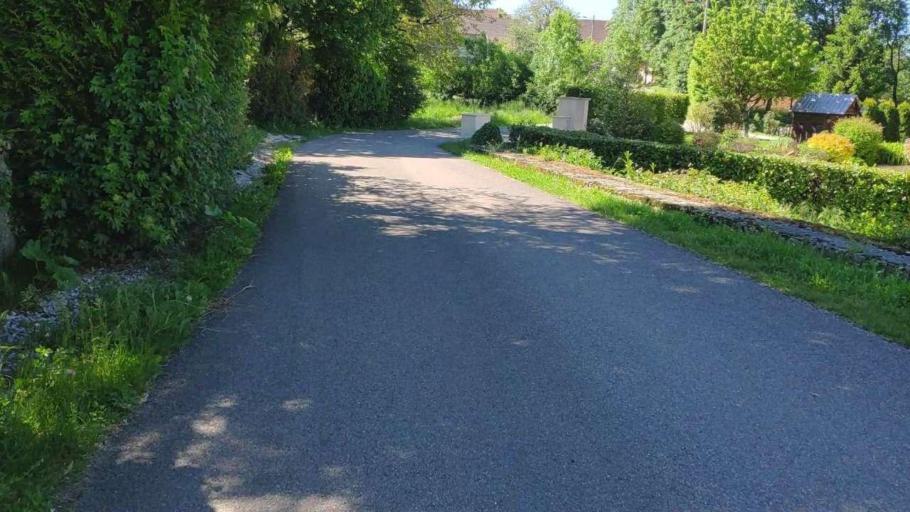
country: FR
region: Franche-Comte
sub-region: Departement du Jura
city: Clairvaux-les-Lacs
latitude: 46.6984
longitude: 5.7249
